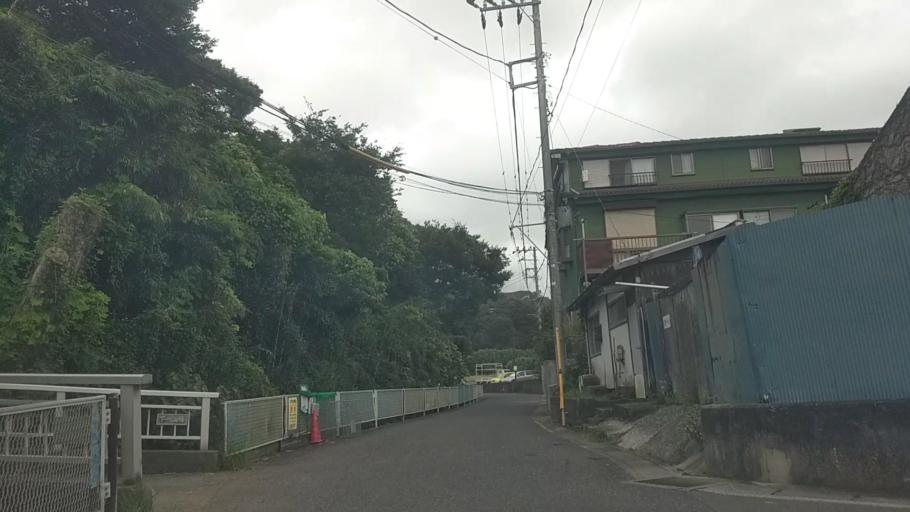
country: JP
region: Kanagawa
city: Hayama
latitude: 35.2305
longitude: 139.6242
